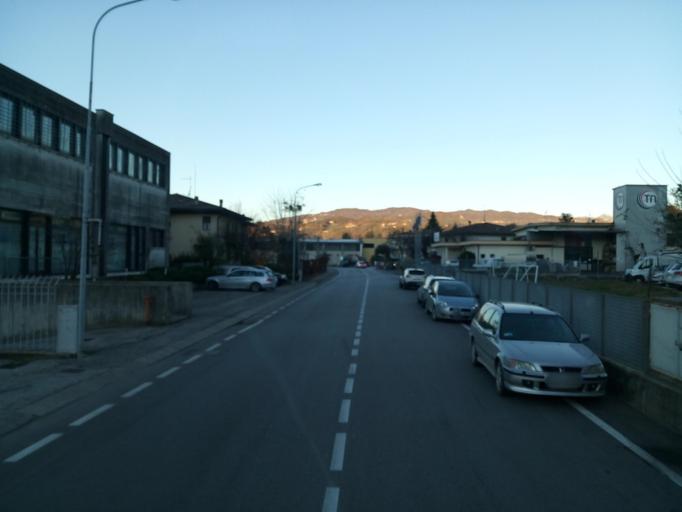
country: IT
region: Veneto
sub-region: Provincia di Vicenza
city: Trissino
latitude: 45.5575
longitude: 11.3808
